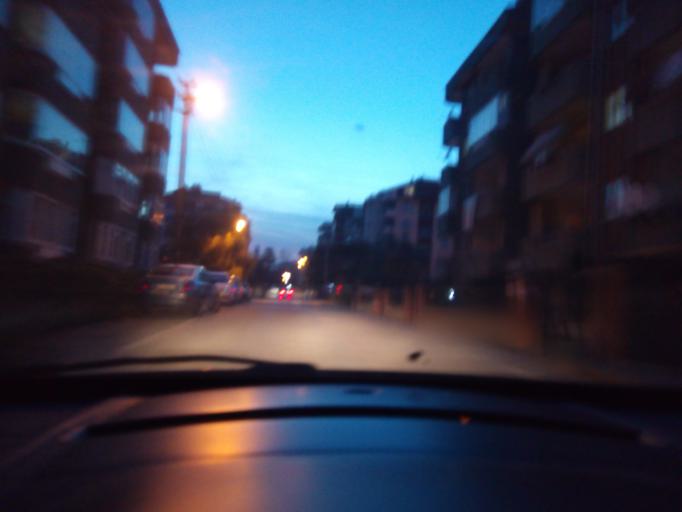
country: TR
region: Bursa
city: Yildirim
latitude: 40.2275
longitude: 28.9855
